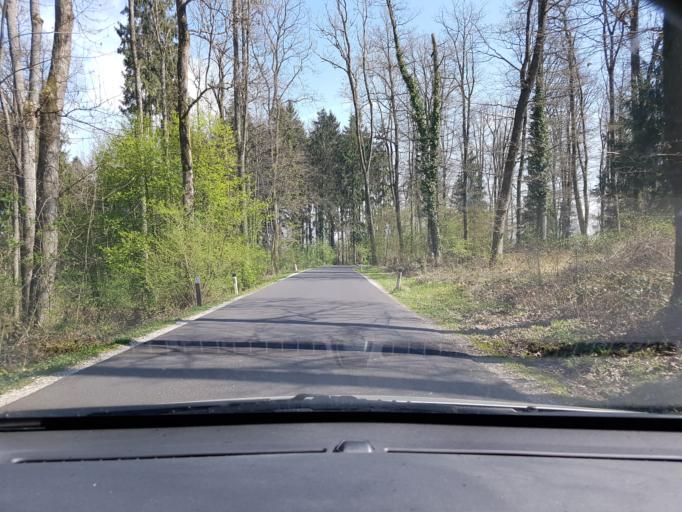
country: AT
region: Upper Austria
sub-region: Politischer Bezirk Linz-Land
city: Sankt Florian
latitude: 48.2066
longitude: 14.3524
